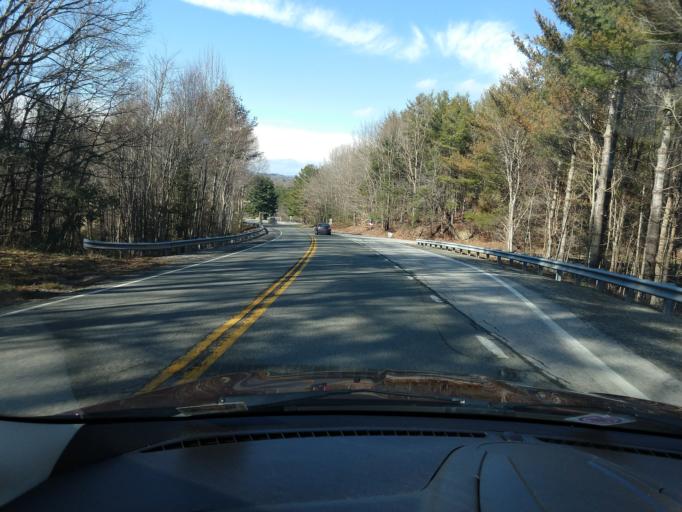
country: US
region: Virginia
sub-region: Floyd County
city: Floyd
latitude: 36.9495
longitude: -80.3596
